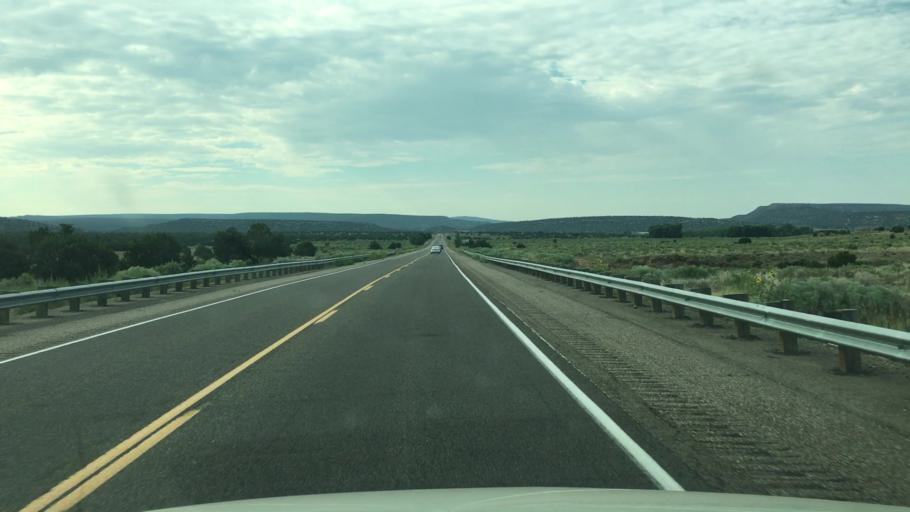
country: US
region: New Mexico
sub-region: Santa Fe County
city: Eldorado at Santa Fe
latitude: 35.4117
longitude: -105.8670
